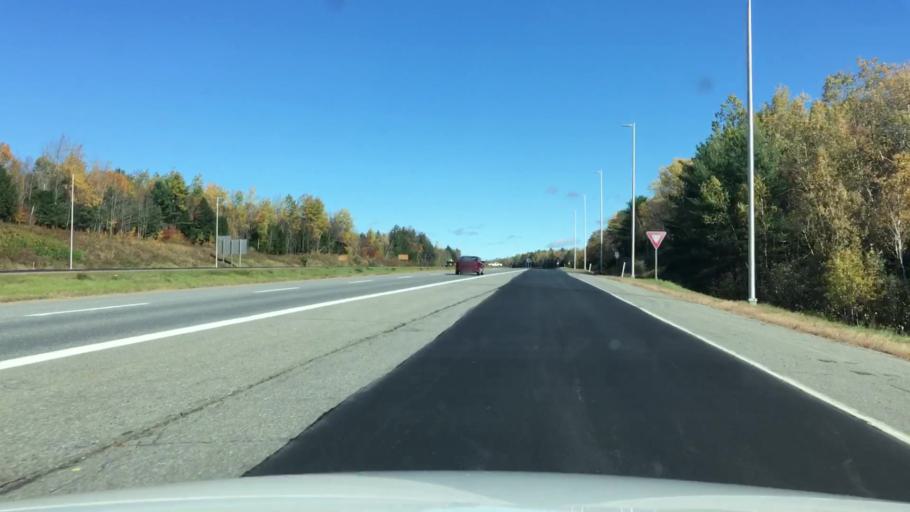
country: US
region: Maine
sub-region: Penobscot County
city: Medway
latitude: 45.6090
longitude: -68.5191
